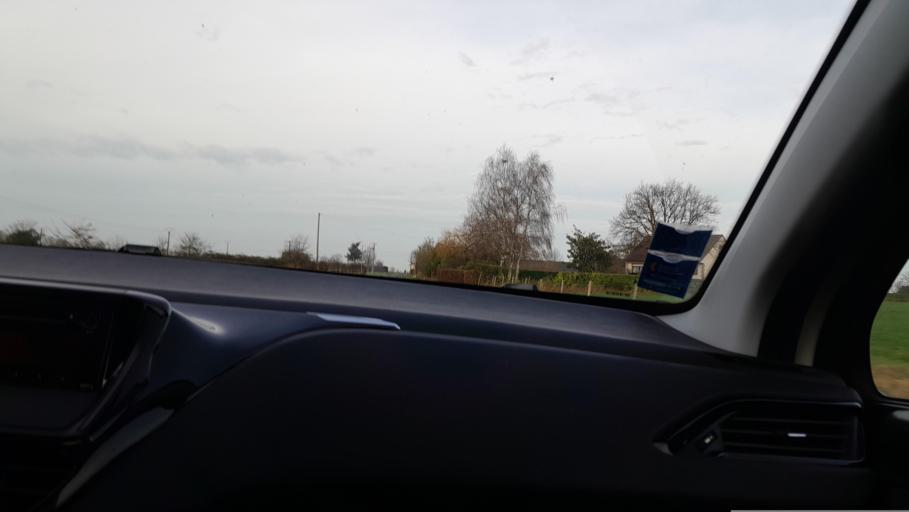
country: FR
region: Pays de la Loire
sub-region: Departement de la Mayenne
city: Craon
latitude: 47.8607
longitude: -0.9789
